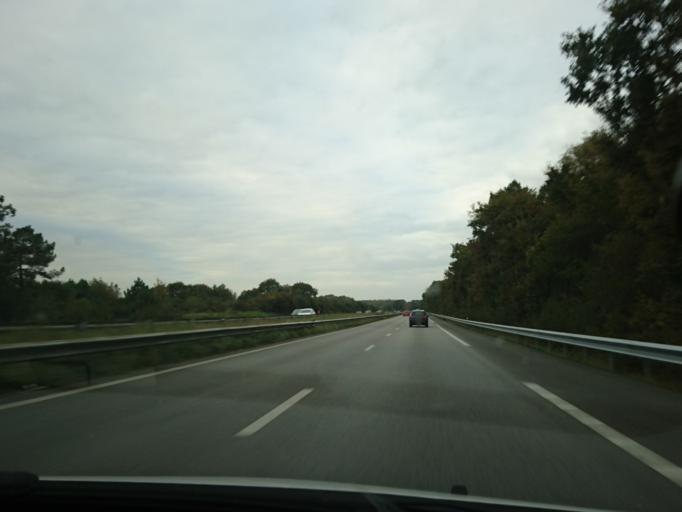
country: FR
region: Brittany
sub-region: Departement du Morbihan
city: Landaul
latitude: 47.7133
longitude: -3.0558
